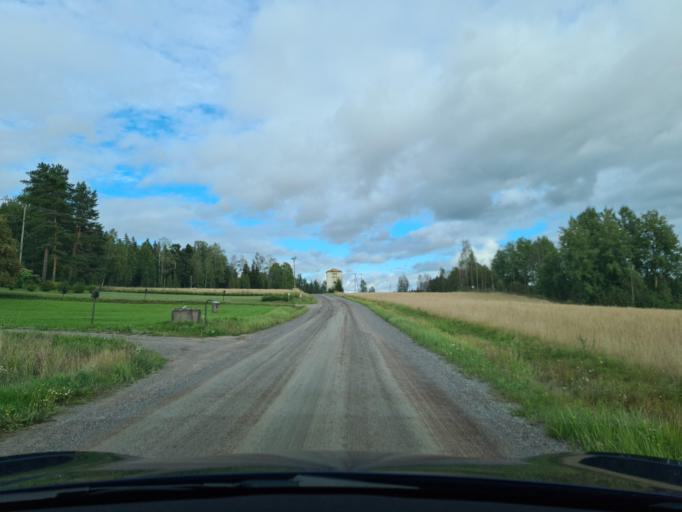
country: FI
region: Uusimaa
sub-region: Helsinki
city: Vihti
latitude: 60.4092
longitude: 24.4952
